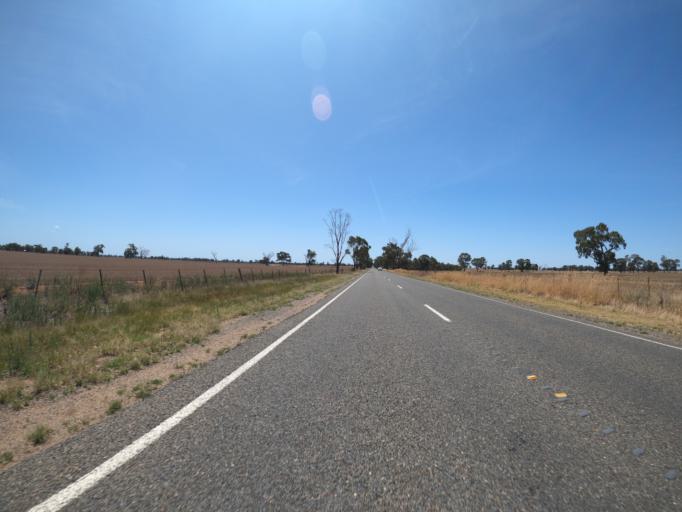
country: AU
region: Victoria
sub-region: Moira
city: Yarrawonga
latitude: -36.0727
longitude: 145.9954
